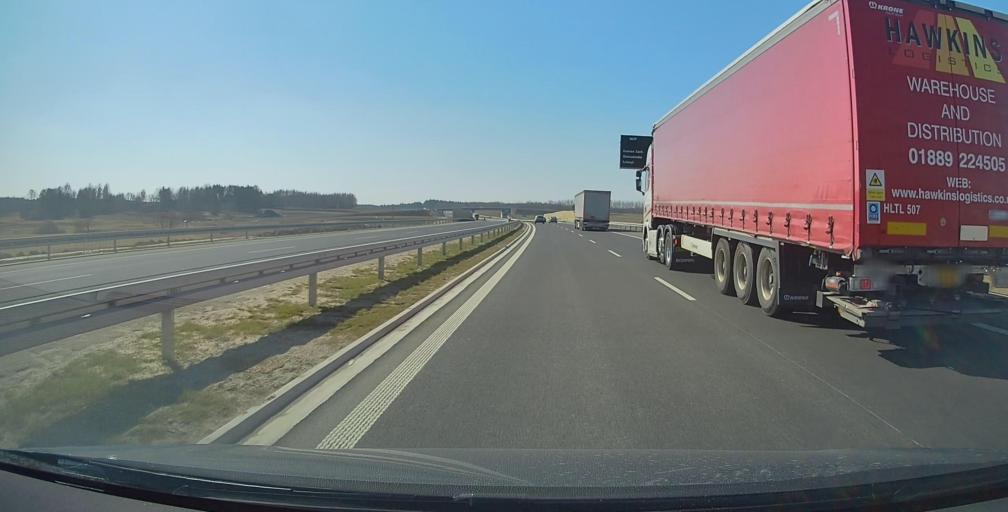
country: PL
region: Subcarpathian Voivodeship
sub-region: Powiat rzeszowski
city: Gorno
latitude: 50.2966
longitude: 22.1188
